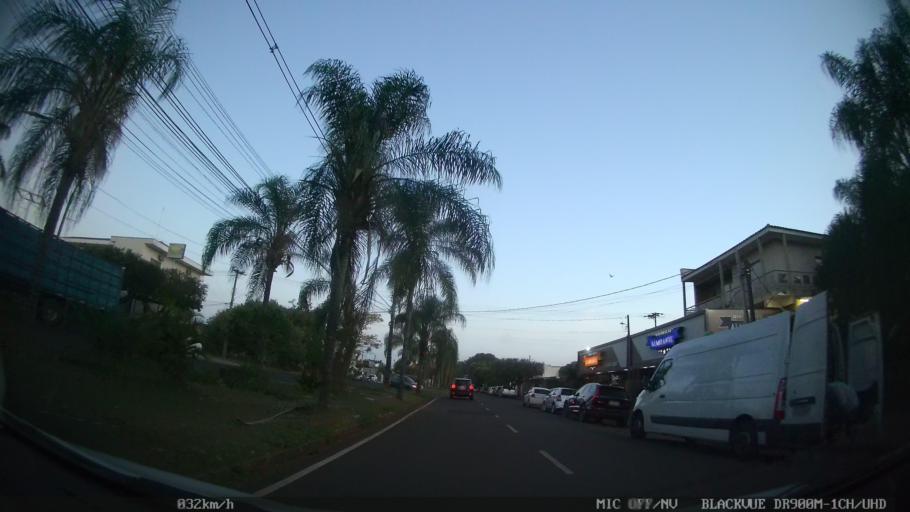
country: BR
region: Sao Paulo
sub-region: Sao Jose Do Rio Preto
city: Sao Jose do Rio Preto
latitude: -20.8035
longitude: -49.3485
